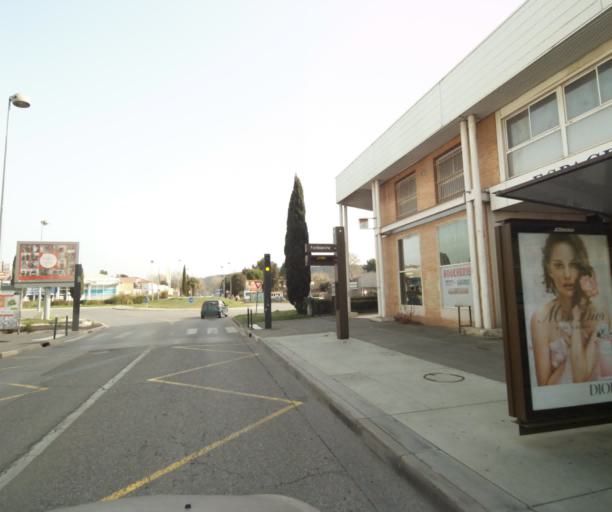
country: FR
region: Provence-Alpes-Cote d'Azur
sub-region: Departement des Bouches-du-Rhone
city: Les Pennes-Mirabeau
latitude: 43.4223
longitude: 5.2862
